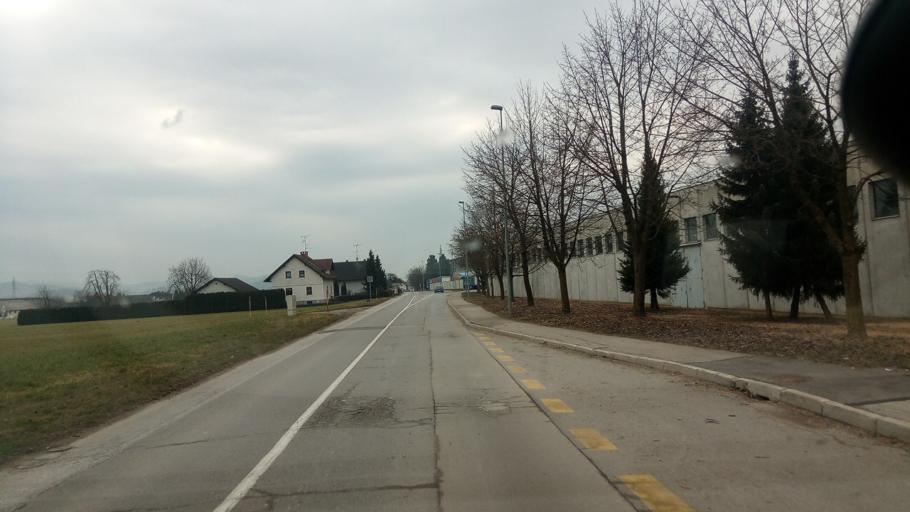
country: SI
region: Domzale
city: Radomlje
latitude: 46.1650
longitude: 14.6085
